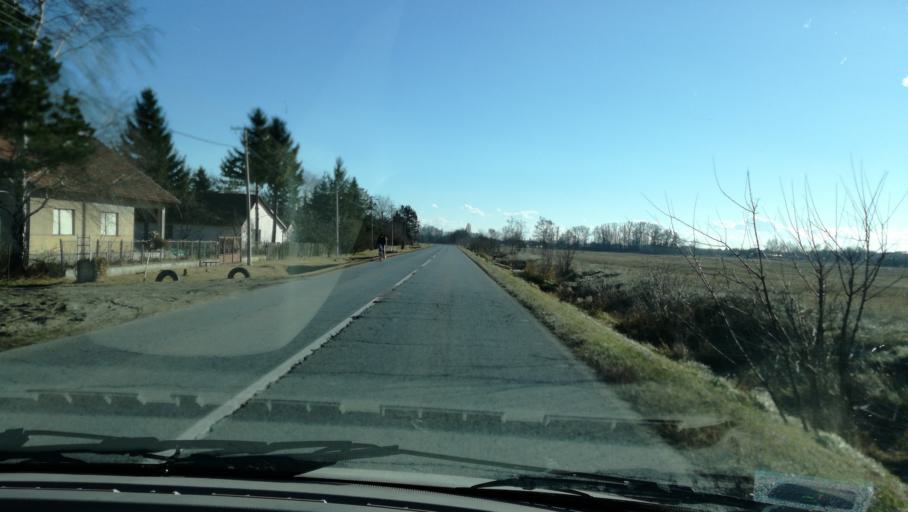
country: HU
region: Csongrad
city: Asotthalom
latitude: 46.1091
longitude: 19.8433
